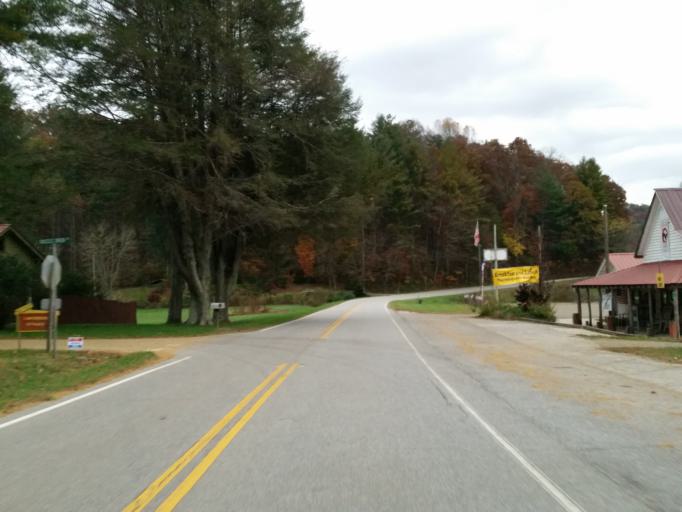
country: US
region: Georgia
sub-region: Union County
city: Blairsville
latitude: 34.7199
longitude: -84.0671
